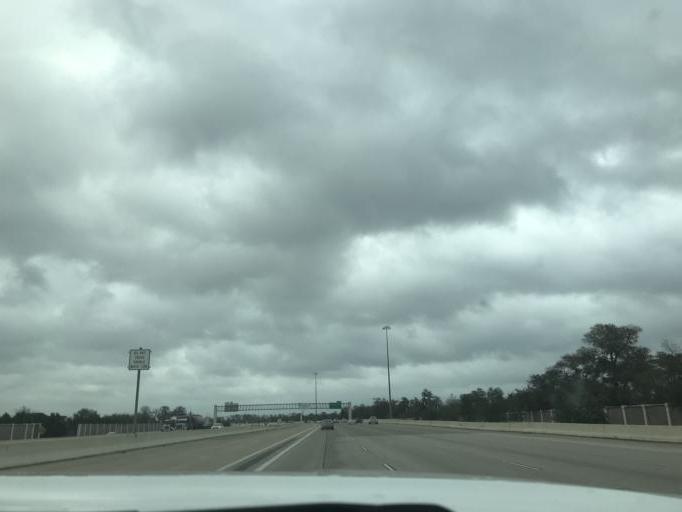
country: US
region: Texas
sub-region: Fort Bend County
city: Greatwood
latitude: 29.5637
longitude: -95.6784
